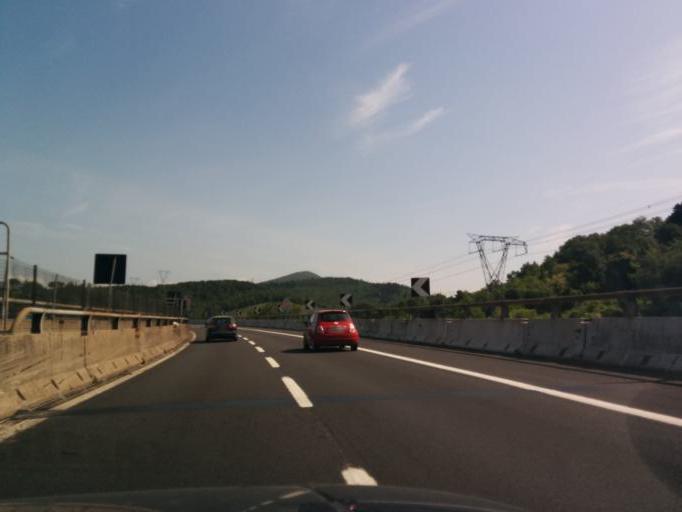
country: IT
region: Tuscany
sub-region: Province of Florence
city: Carraia
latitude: 43.8827
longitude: 11.1843
